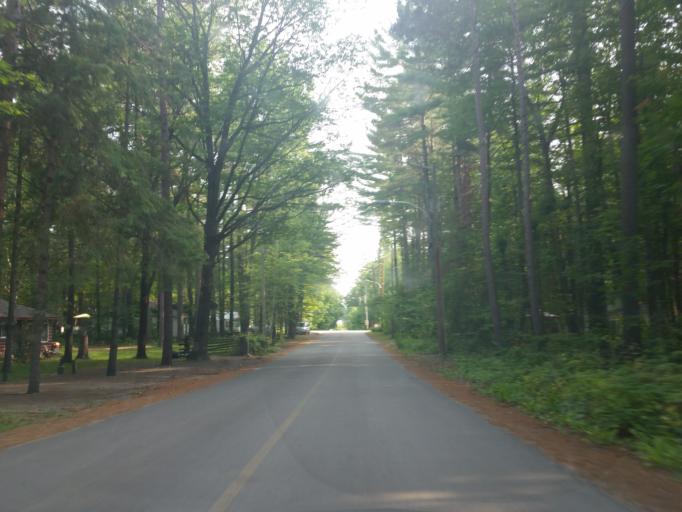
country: CA
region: Quebec
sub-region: Outaouais
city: Shawville
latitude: 45.5220
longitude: -76.4264
